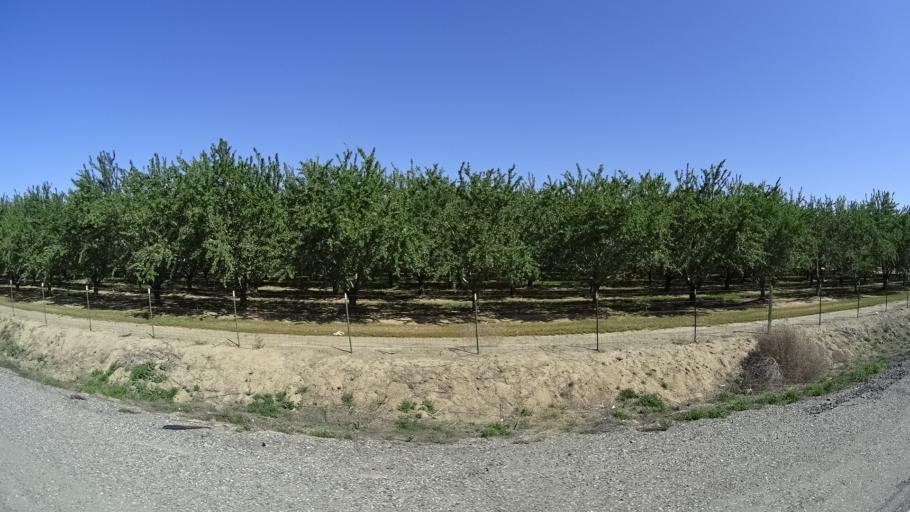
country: US
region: California
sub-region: Glenn County
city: Hamilton City
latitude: 39.7091
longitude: -122.0383
